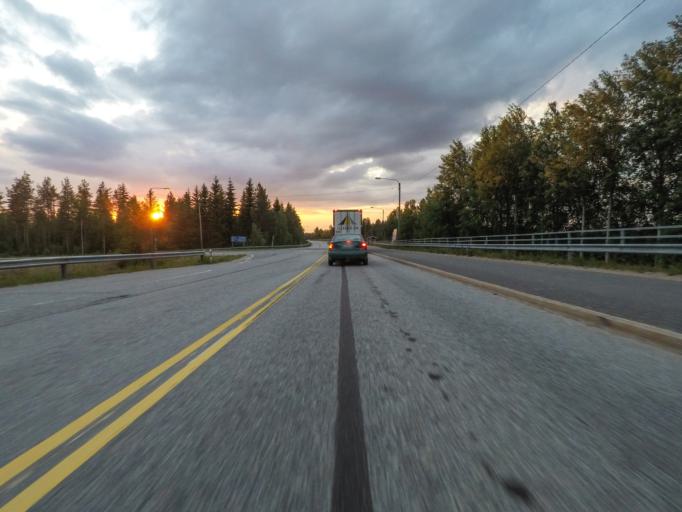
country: FI
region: Central Finland
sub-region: Jyvaeskylae
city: Hankasalmi
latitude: 62.3123
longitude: 26.4944
